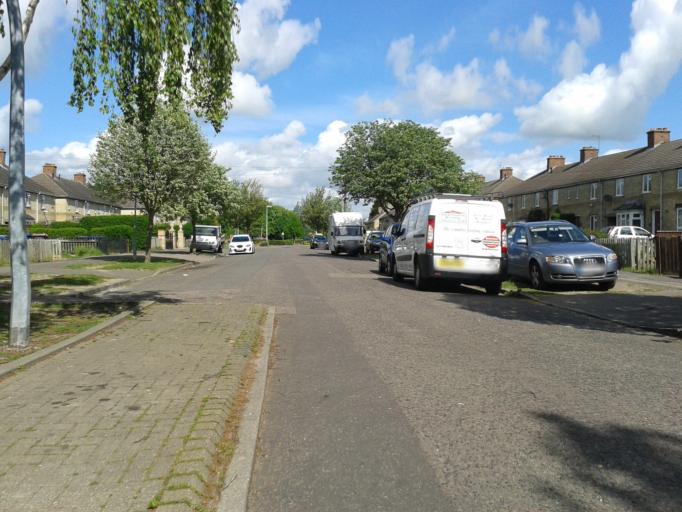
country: GB
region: England
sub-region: Cambridgeshire
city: Cambridge
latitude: 52.2223
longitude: 0.1514
